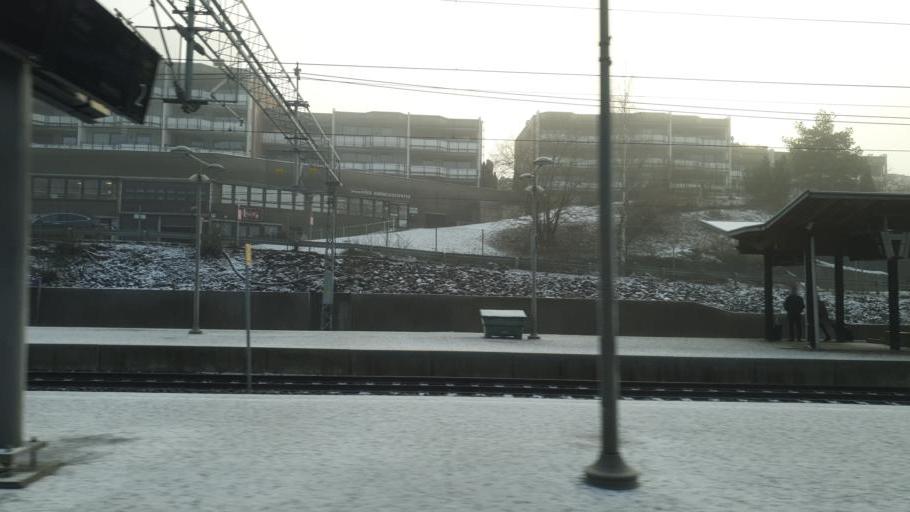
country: NO
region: Akershus
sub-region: Baerum
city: Sandvika
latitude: 59.8933
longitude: 10.5268
